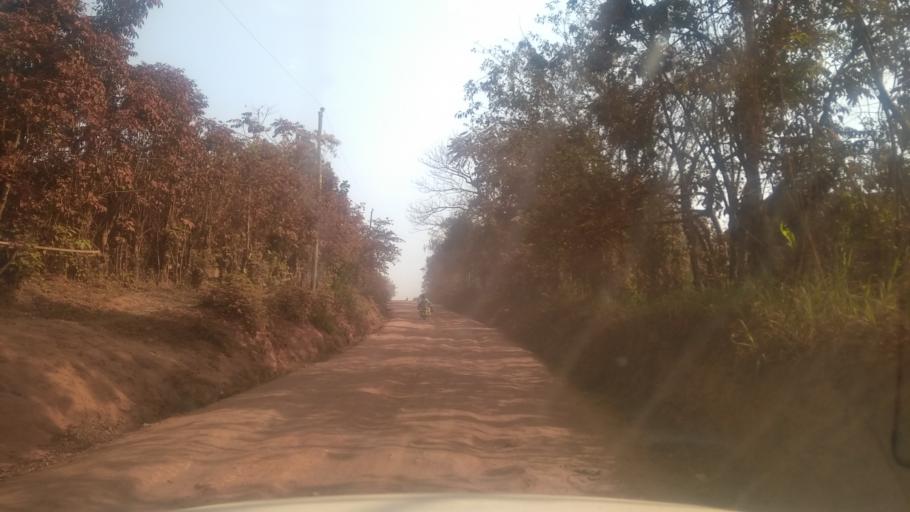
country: CM
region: West
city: Bafoussam
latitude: 5.5156
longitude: 10.4095
